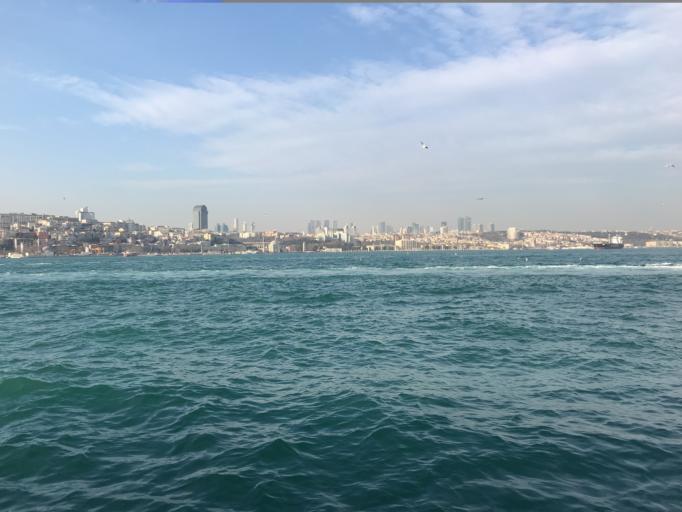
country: TR
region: Istanbul
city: Eminoenue
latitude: 41.0225
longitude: 28.9957
